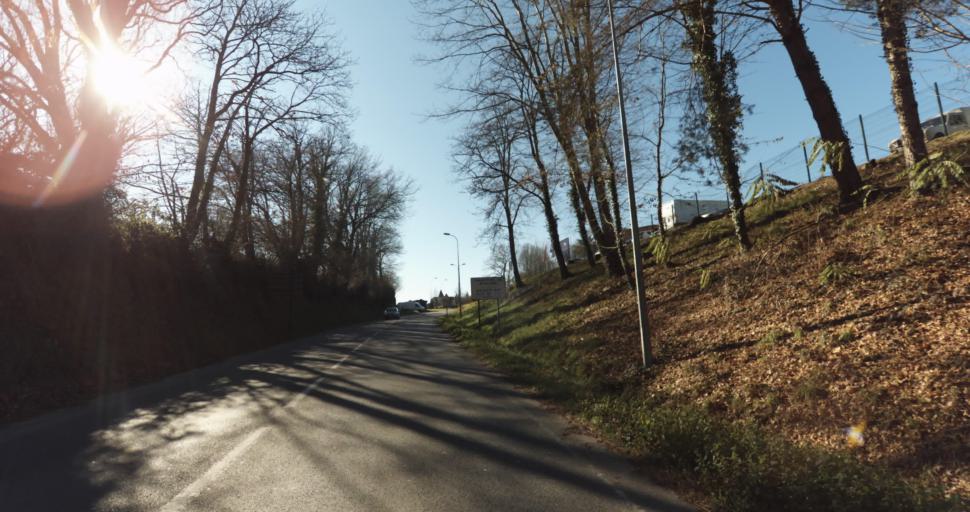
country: FR
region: Aquitaine
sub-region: Departement des Pyrenees-Atlantiques
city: Morlaas
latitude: 43.3521
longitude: -0.2554
